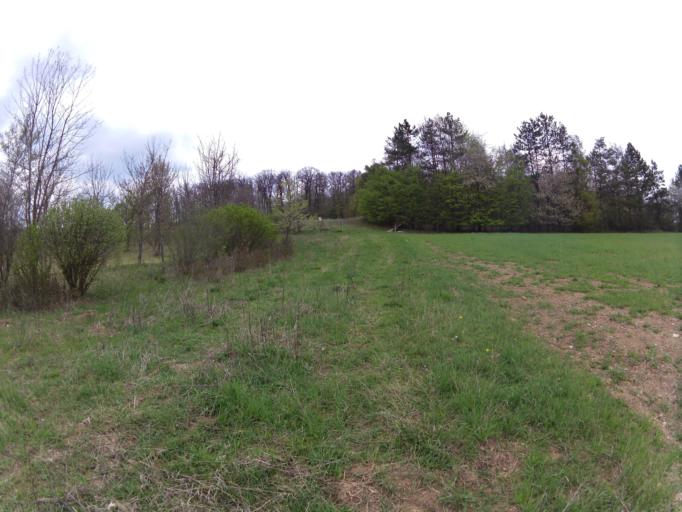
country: DE
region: Bavaria
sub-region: Regierungsbezirk Unterfranken
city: Greussenheim
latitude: 49.8246
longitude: 9.7798
